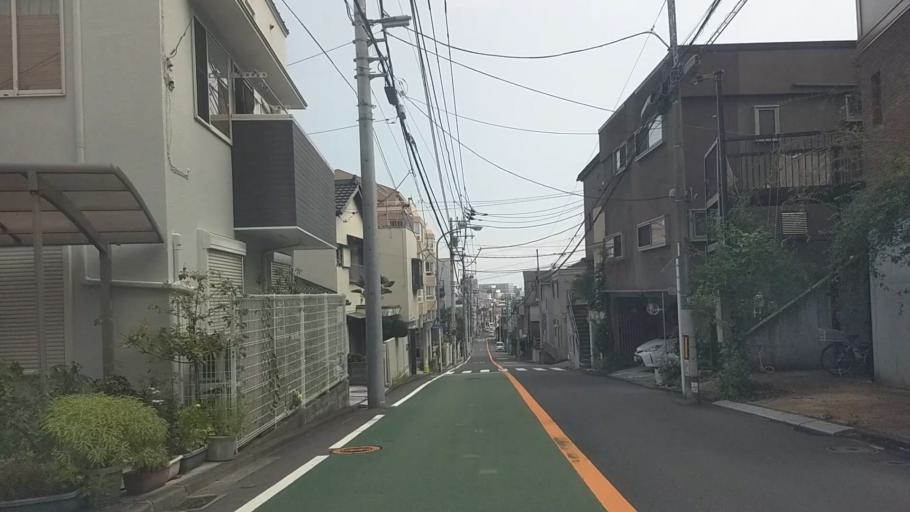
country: JP
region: Kanagawa
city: Yokohama
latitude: 35.4947
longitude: 139.6380
